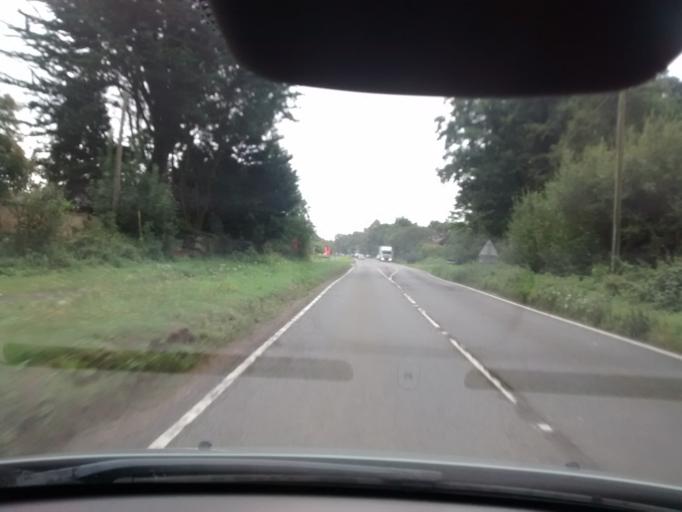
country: GB
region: England
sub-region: Hampshire
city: Ringwood
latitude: 50.8606
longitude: -1.7888
